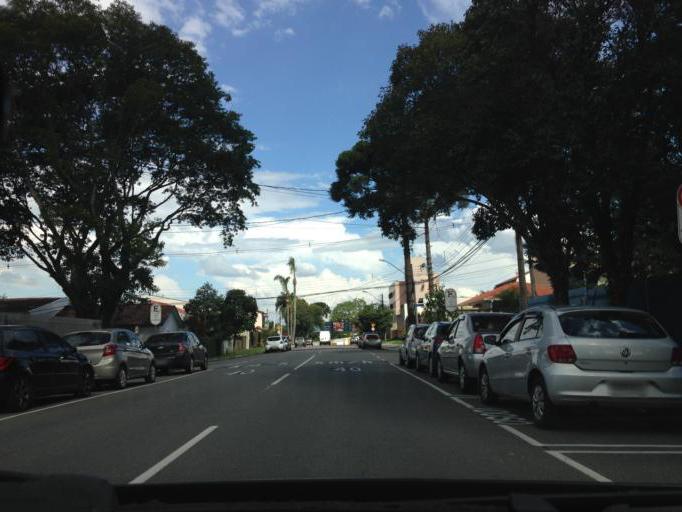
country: BR
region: Parana
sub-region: Curitiba
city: Curitiba
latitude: -25.4096
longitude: -49.2388
